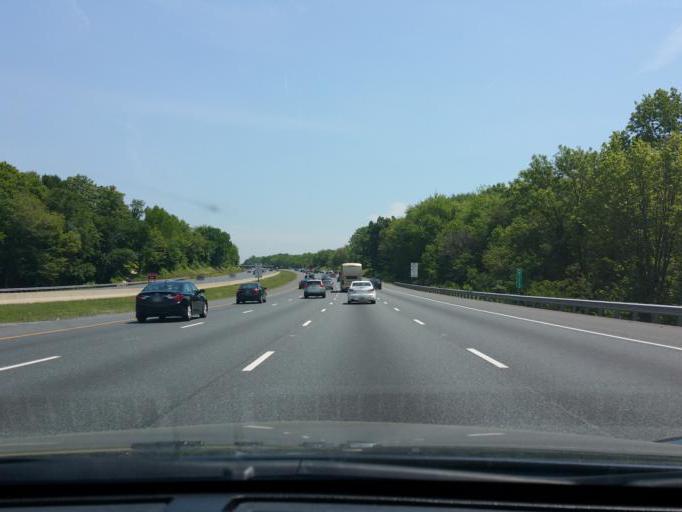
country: US
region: Maryland
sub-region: Baltimore County
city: Kingsville
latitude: 39.4227
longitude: -76.3978
